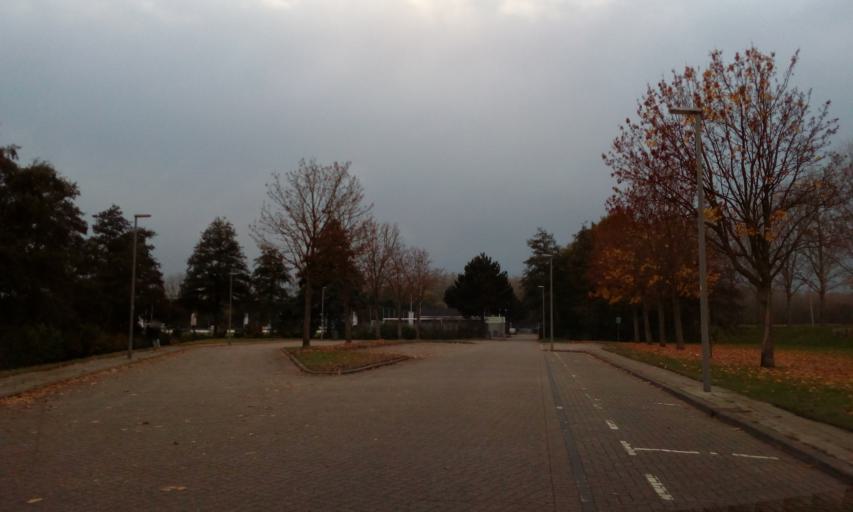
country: NL
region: South Holland
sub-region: Gemeente Capelle aan den IJssel
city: Capelle aan den IJssel
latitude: 51.9694
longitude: 4.5610
